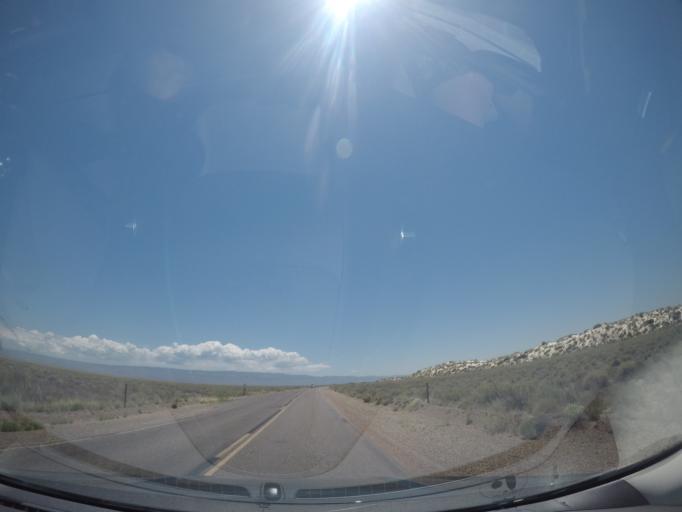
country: US
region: New Mexico
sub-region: Otero County
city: Holloman Air Force Base
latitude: 32.7876
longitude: -106.1869
